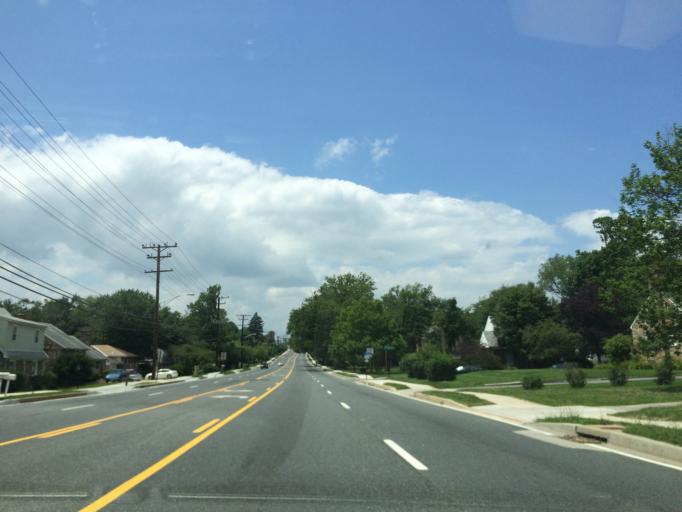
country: US
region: Maryland
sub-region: Baltimore County
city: Randallstown
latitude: 39.3653
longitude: -76.7893
